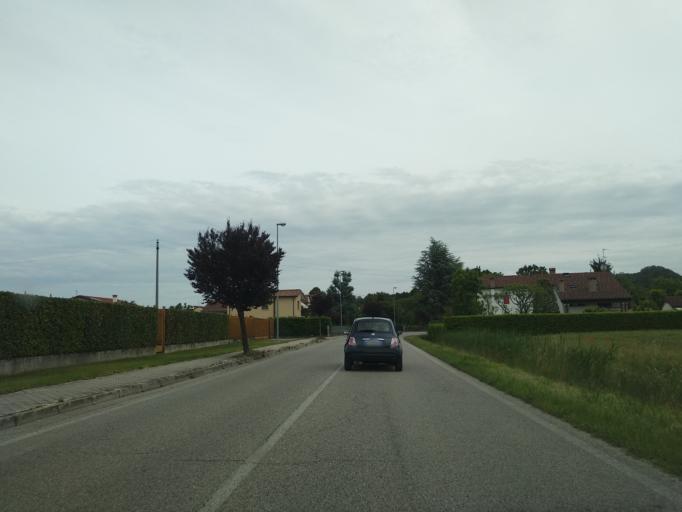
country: IT
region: Veneto
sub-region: Provincia di Padova
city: Montemerlo
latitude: 45.3876
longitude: 11.7023
